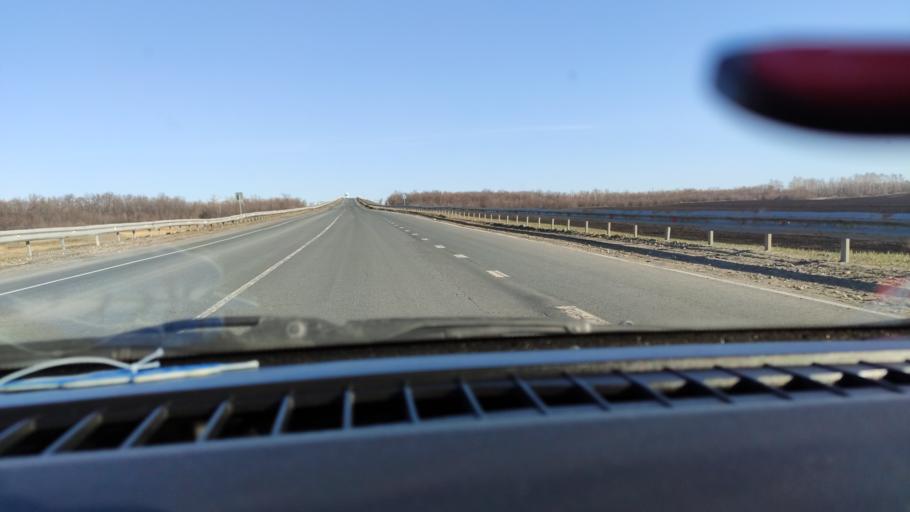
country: RU
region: Saratov
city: Dukhovnitskoye
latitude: 52.7480
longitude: 48.2505
